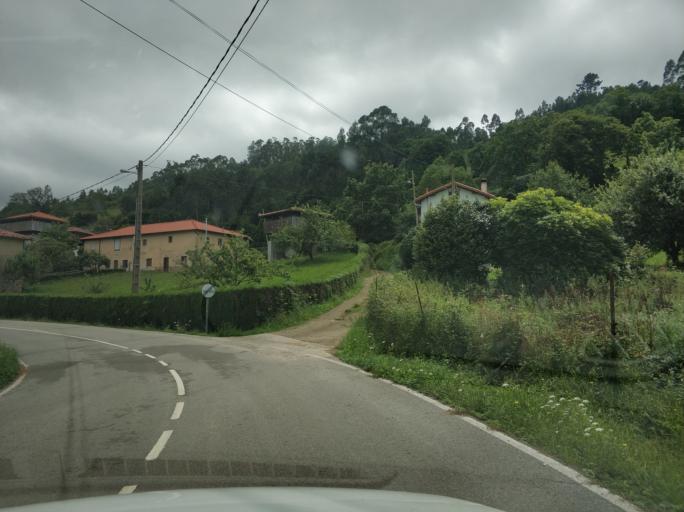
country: ES
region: Asturias
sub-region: Province of Asturias
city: Cudillero
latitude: 43.5422
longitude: -6.2388
